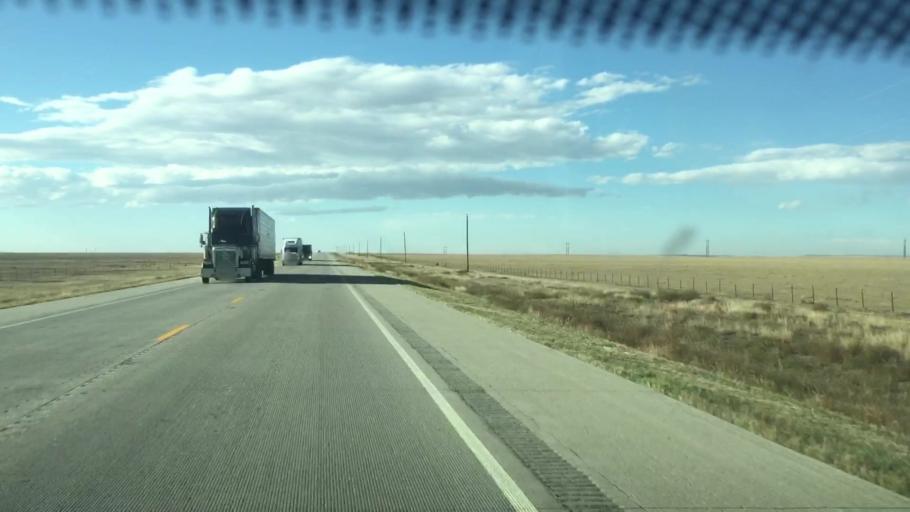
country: US
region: Colorado
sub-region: Lincoln County
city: Hugo
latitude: 39.0816
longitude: -103.3888
